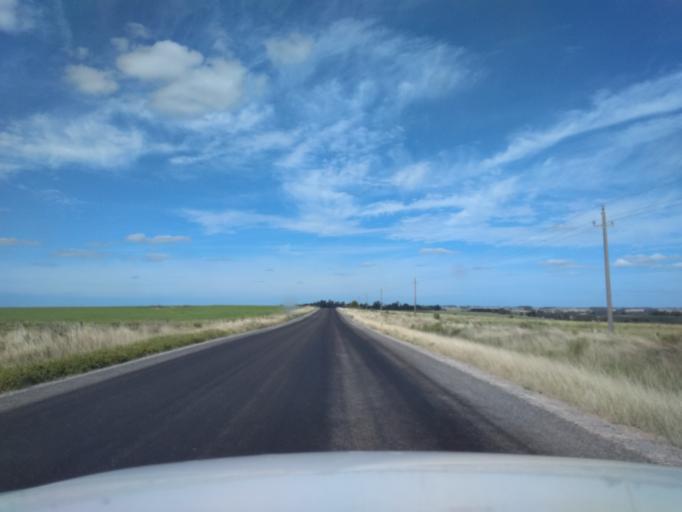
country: UY
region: Florida
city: Casupa
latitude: -34.0301
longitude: -55.8733
